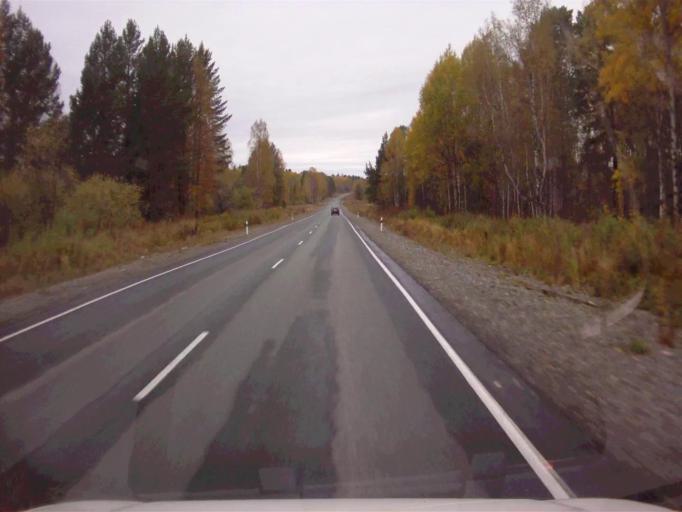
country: RU
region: Chelyabinsk
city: Nyazepetrovsk
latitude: 56.0451
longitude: 59.7600
